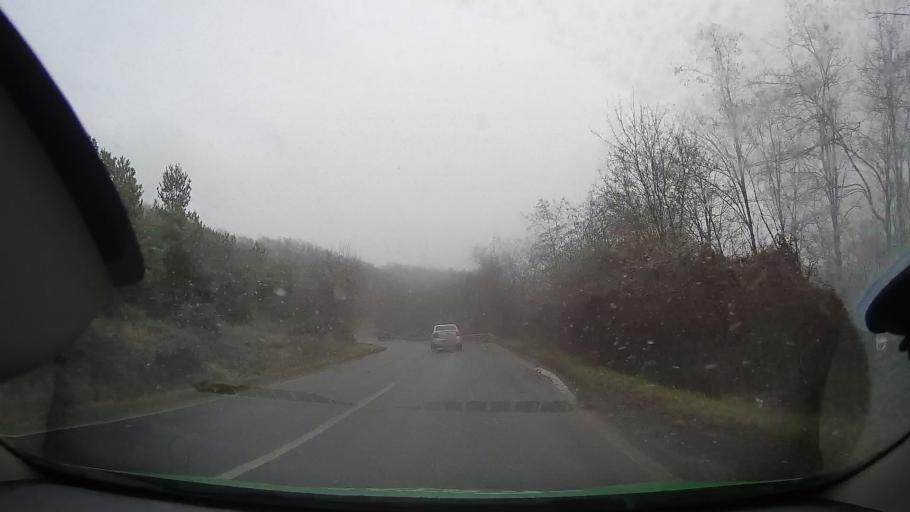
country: RO
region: Sibiu
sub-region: Municipiul Medias
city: Medias
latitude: 46.1851
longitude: 24.3285
